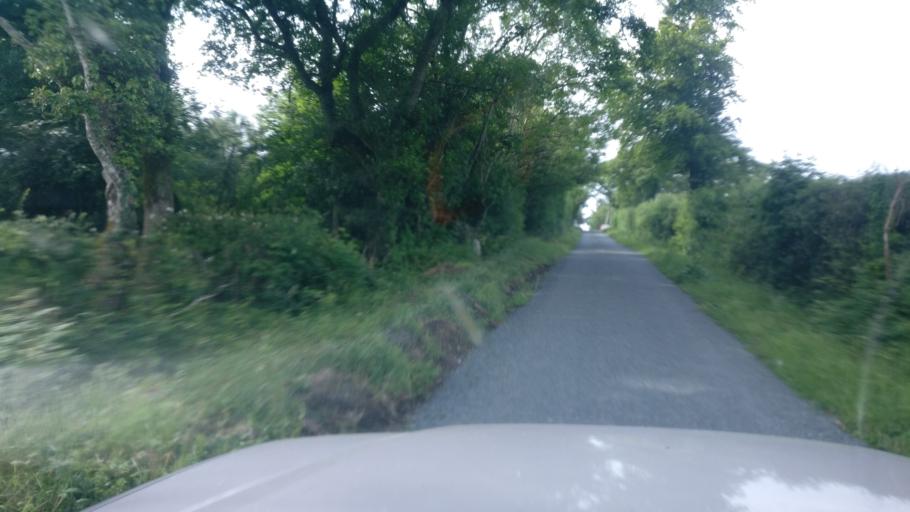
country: IE
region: Connaught
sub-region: County Galway
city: Gort
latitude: 53.1066
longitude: -8.7148
